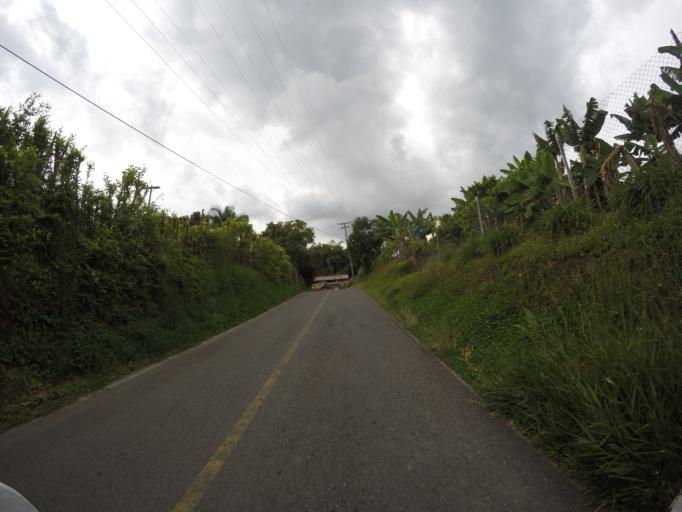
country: CO
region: Quindio
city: Quimbaya
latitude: 4.6082
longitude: -75.7189
